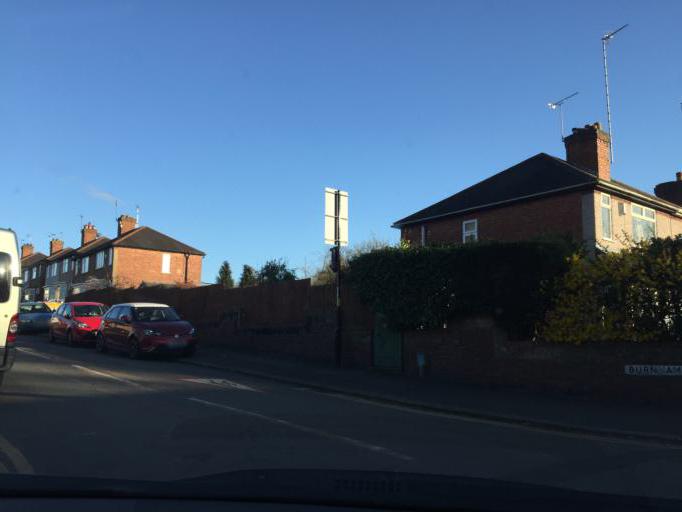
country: GB
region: England
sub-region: Coventry
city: Coventry
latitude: 52.3888
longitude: -1.4861
